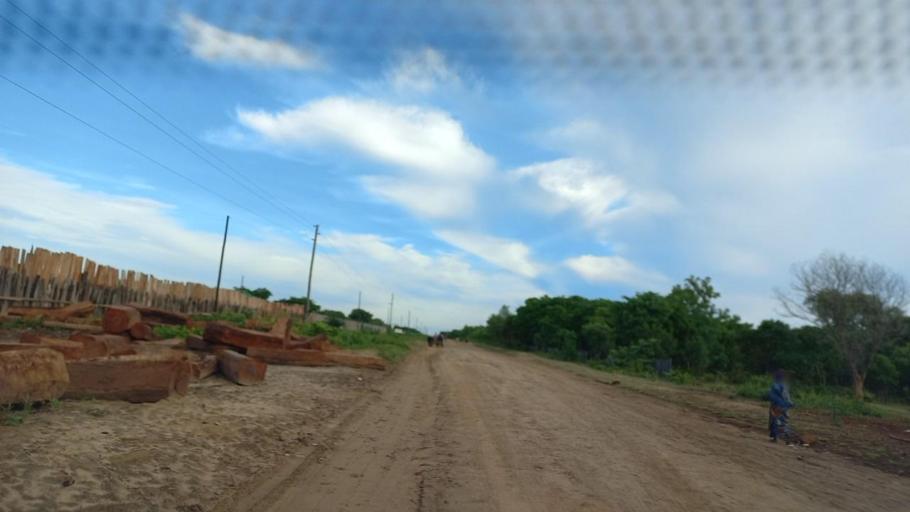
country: ZM
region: North-Western
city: Kabompo
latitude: -13.4194
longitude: 24.3214
